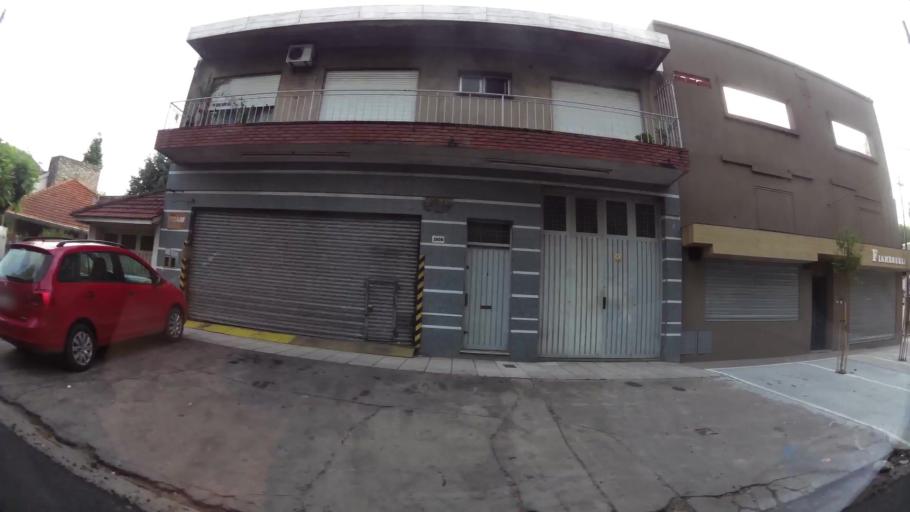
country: AR
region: Buenos Aires
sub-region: Partido de Quilmes
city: Quilmes
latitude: -34.7357
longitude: -58.2559
